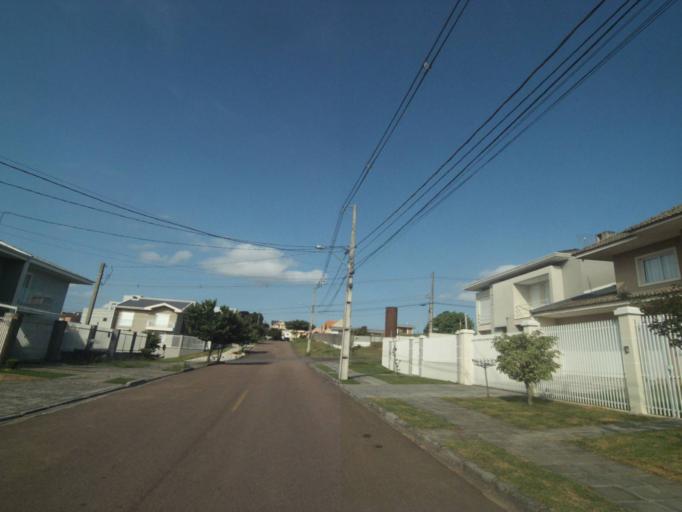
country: BR
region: Parana
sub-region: Pinhais
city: Pinhais
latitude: -25.4097
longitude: -49.2133
